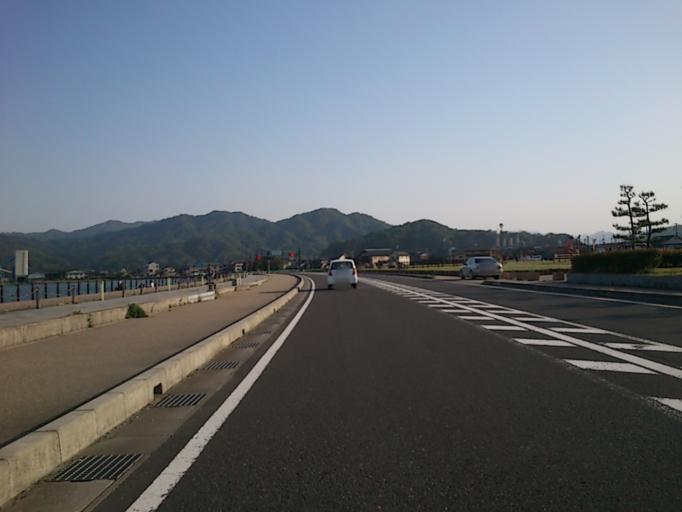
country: JP
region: Kyoto
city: Miyazu
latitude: 35.5668
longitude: 135.1563
